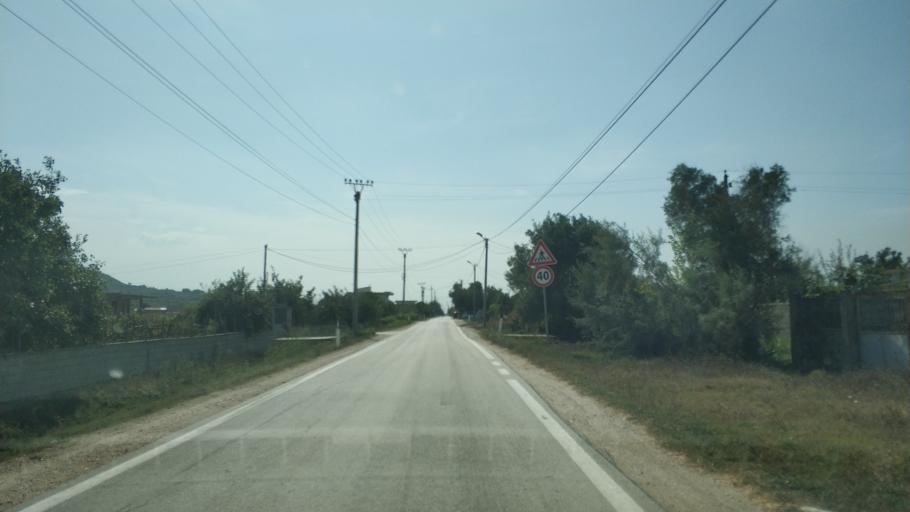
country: AL
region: Fier
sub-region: Rrethi i Fierit
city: Dermenas
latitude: 40.7396
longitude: 19.4792
